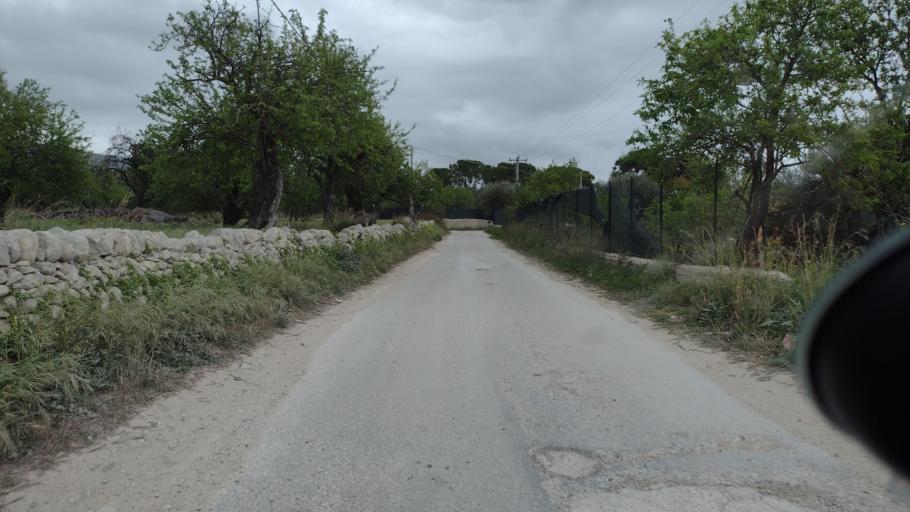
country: IT
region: Sicily
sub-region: Provincia di Siracusa
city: Avola
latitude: 36.9060
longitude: 15.1138
